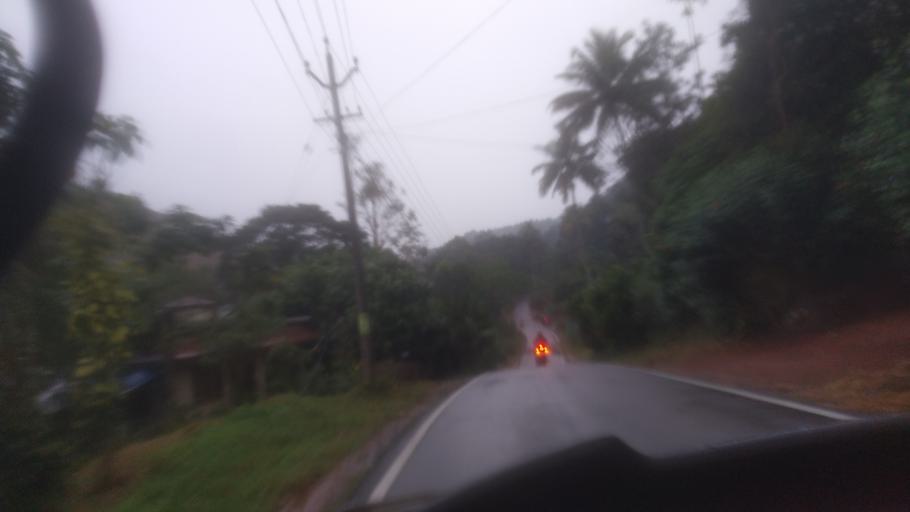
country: IN
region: Kerala
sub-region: Idukki
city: Idukki
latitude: 9.9308
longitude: 77.0695
